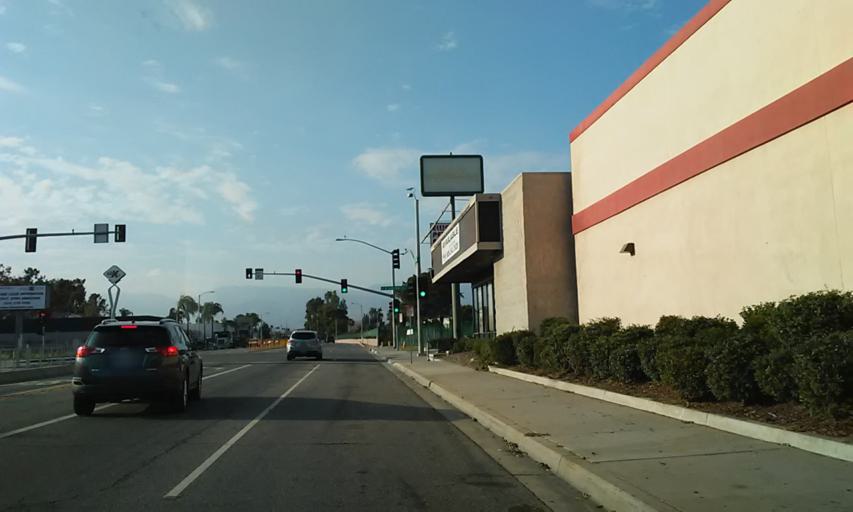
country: US
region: California
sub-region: San Bernardino County
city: Colton
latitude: 34.0850
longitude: -117.2937
